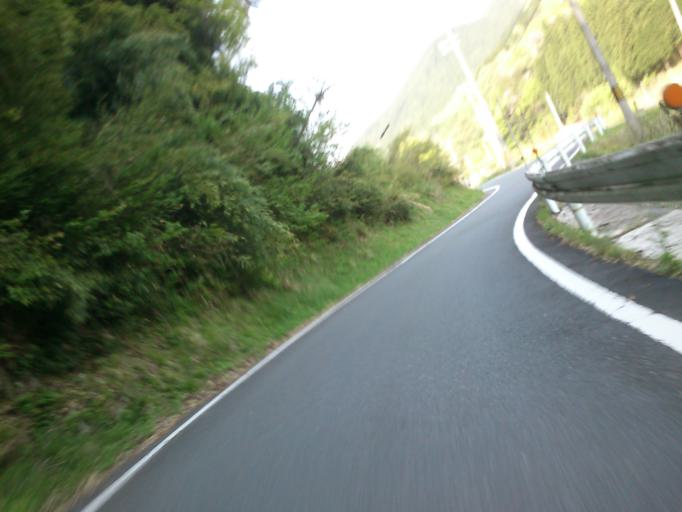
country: JP
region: Kyoto
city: Fukuchiyama
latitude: 35.3507
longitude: 135.0117
